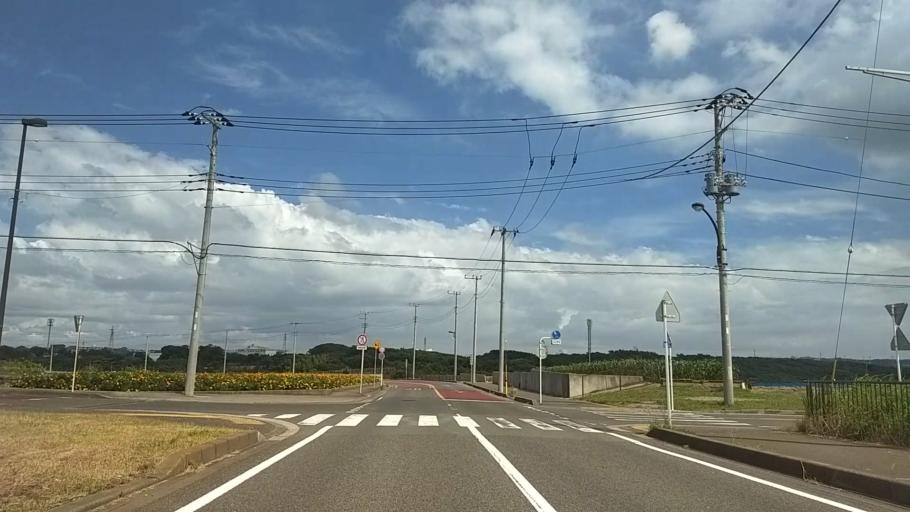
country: JP
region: Kanagawa
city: Miura
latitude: 35.1955
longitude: 139.6147
